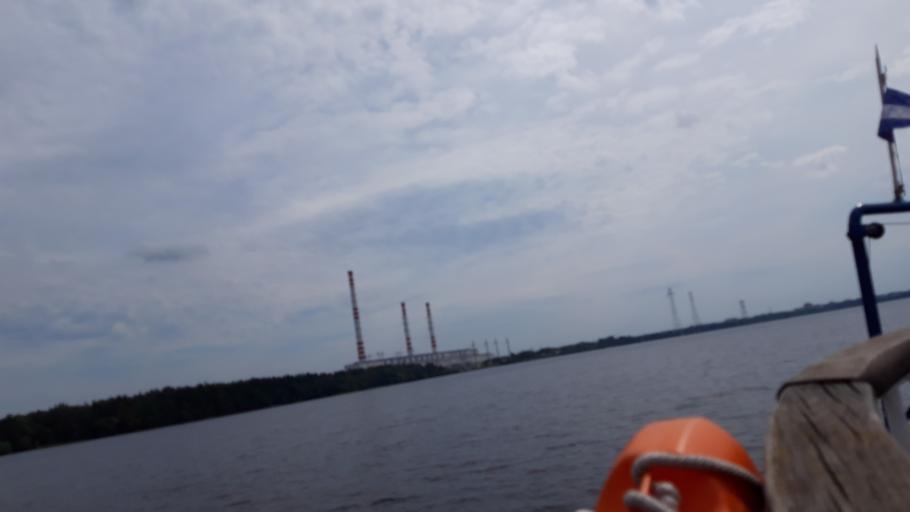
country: RU
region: Tverskaya
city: Konakovo
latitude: 56.7499
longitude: 36.7512
